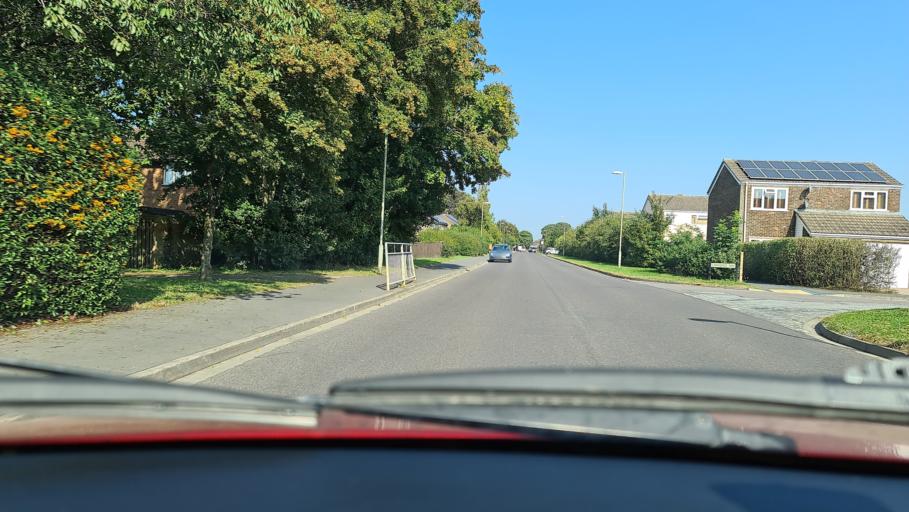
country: GB
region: England
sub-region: Oxfordshire
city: Bicester
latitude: 51.9017
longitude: -1.1733
